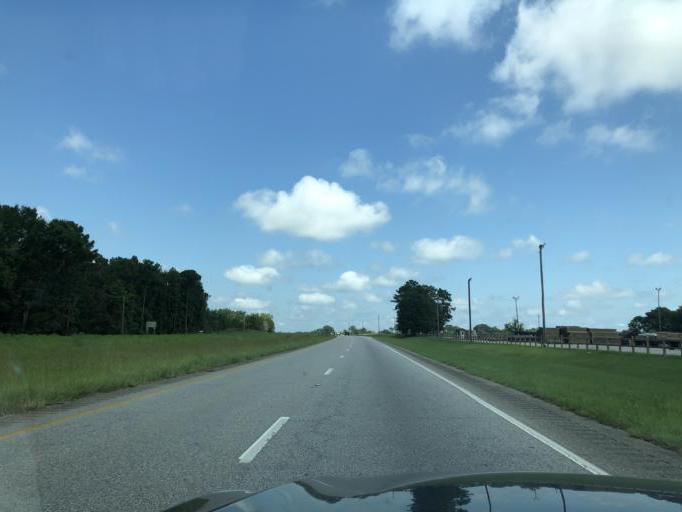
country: US
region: Alabama
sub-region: Henry County
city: Abbeville
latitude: 31.5927
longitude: -85.2775
